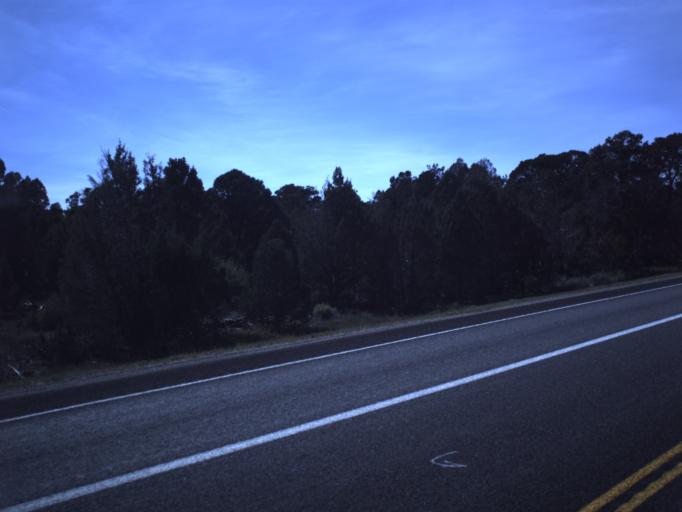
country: US
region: Colorado
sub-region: Dolores County
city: Dove Creek
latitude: 37.8385
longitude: -109.1185
